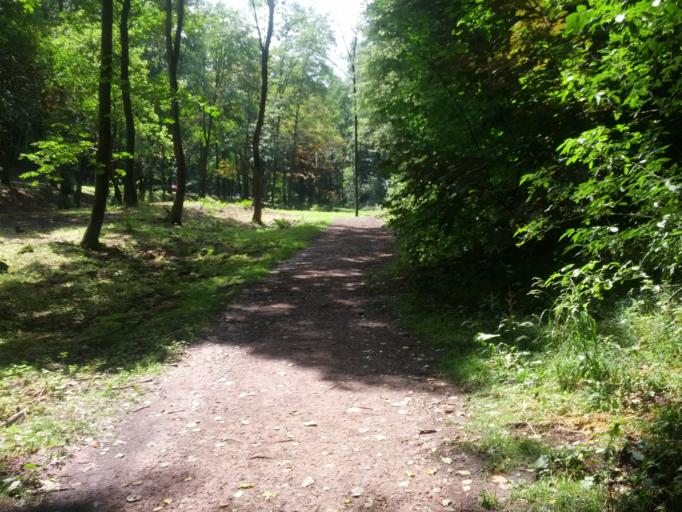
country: DE
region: Thuringia
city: Eisenach
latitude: 50.9567
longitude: 10.3099
